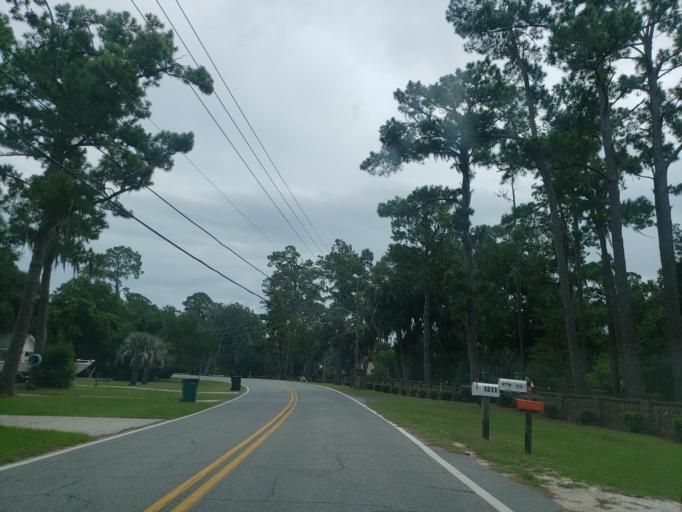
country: US
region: Georgia
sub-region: Chatham County
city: Wilmington Island
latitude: 31.9863
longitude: -80.9891
